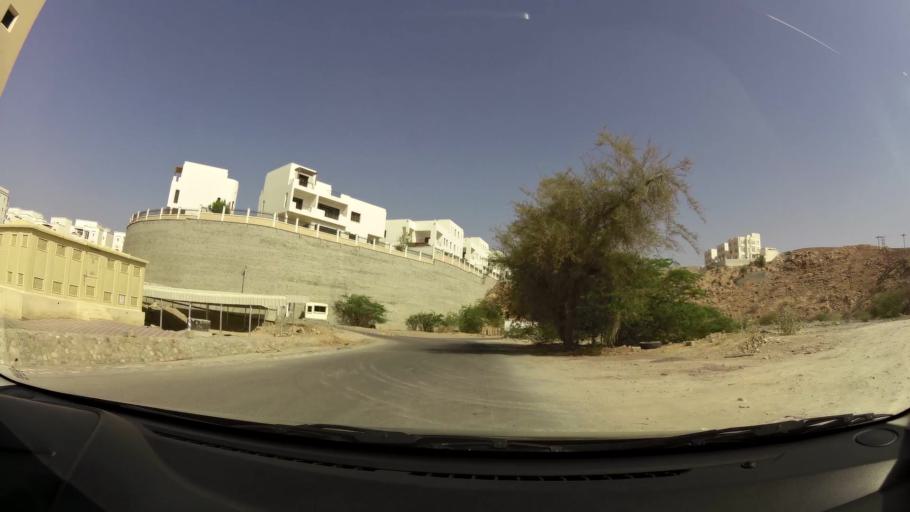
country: OM
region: Muhafazat Masqat
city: Muscat
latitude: 23.6040
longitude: 58.4906
